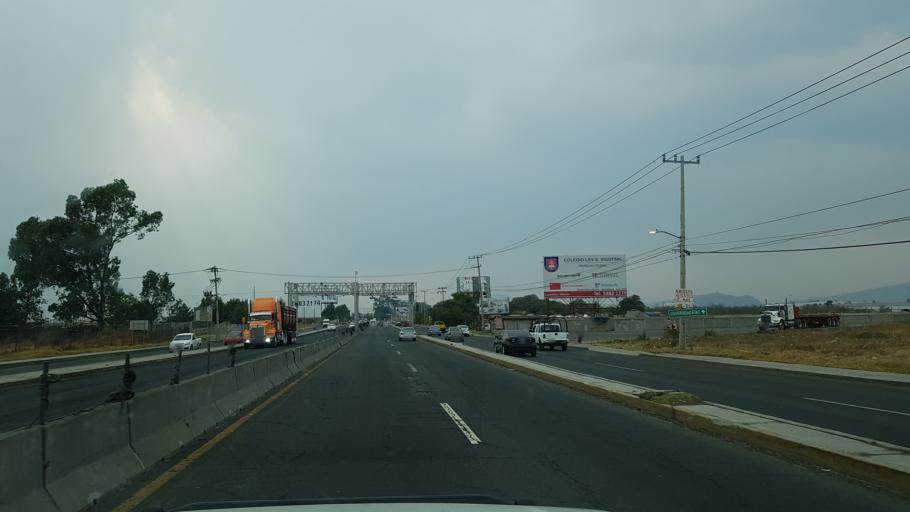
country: MX
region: Mexico
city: Cocotitlan
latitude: 19.2456
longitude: -98.8658
